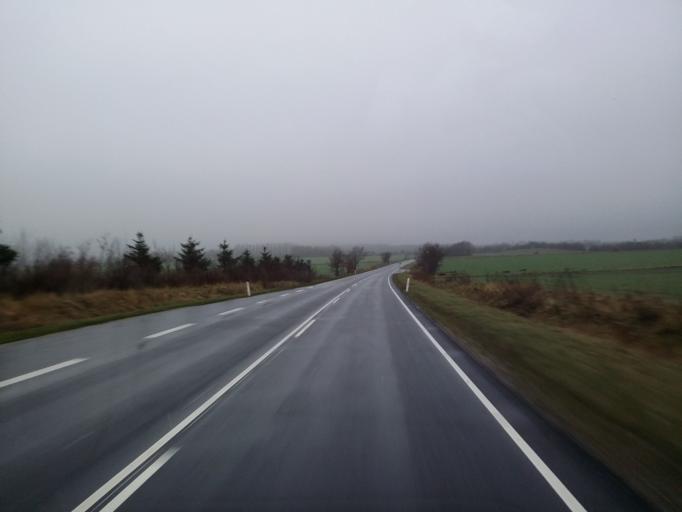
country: DK
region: Capital Region
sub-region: Frederikssund Kommune
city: Jaegerspris
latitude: 55.8236
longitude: 12.0074
